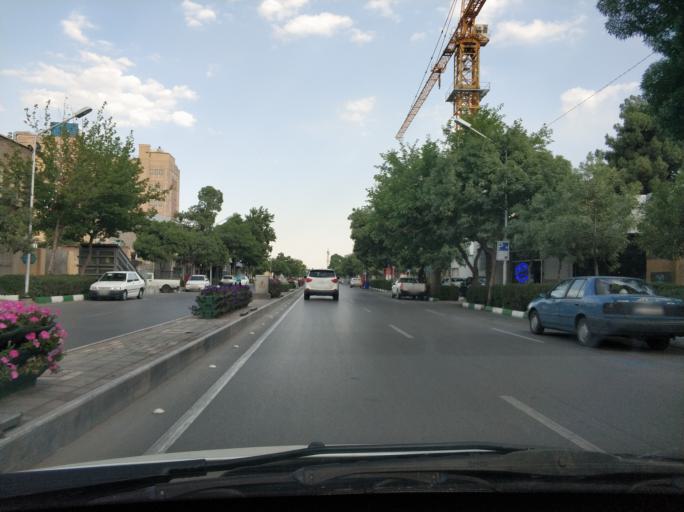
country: IR
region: Razavi Khorasan
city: Mashhad
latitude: 36.2788
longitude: 59.5982
